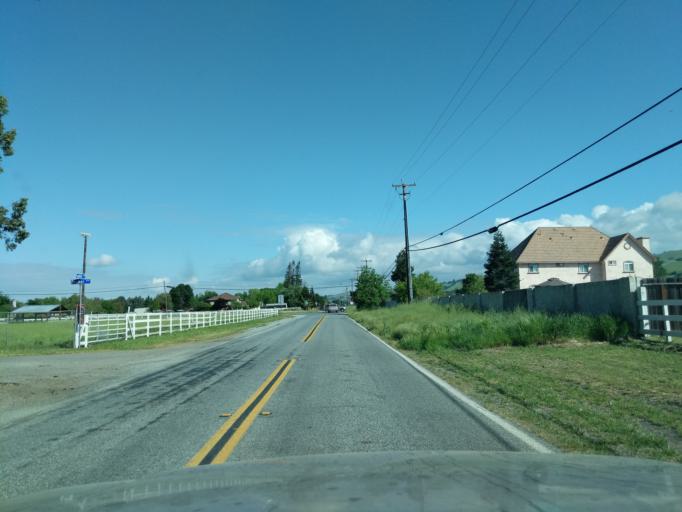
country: US
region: California
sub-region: Santa Clara County
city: San Martin
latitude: 37.0940
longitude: -121.5811
